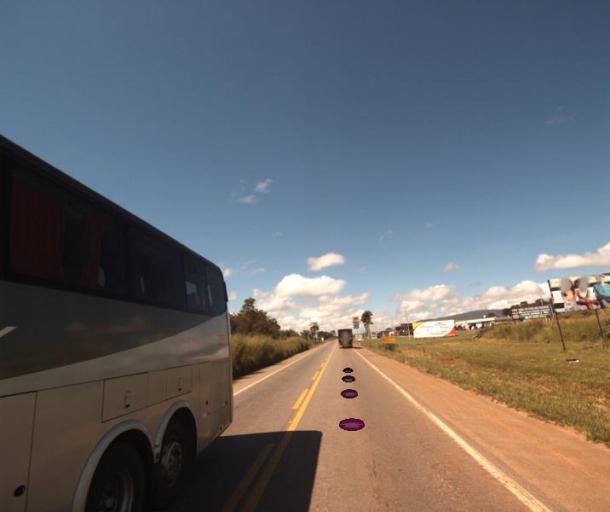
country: BR
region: Goias
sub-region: Jaragua
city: Jaragua
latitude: -15.7286
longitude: -49.3261
